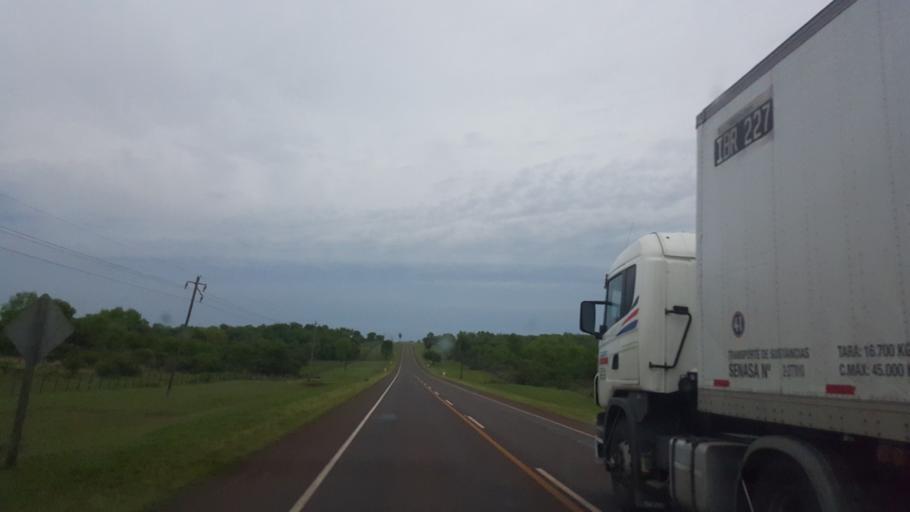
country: AR
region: Misiones
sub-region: Departamento de Apostoles
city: San Jose
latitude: -27.7310
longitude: -55.7881
